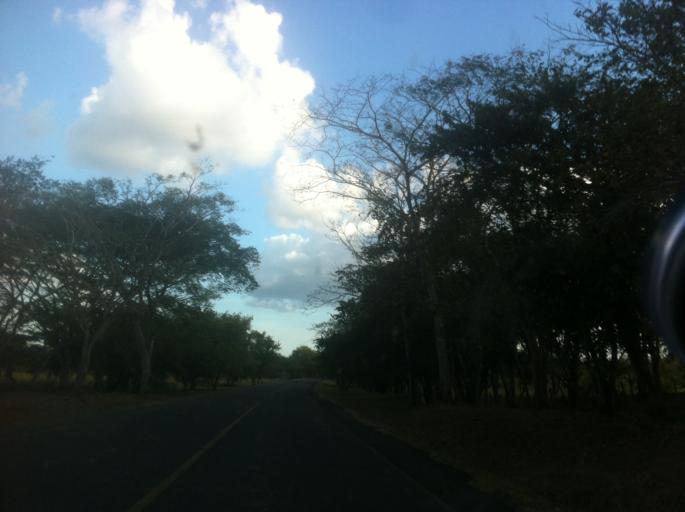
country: NI
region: Rio San Juan
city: El Almendro
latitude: 11.5937
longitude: -84.8507
